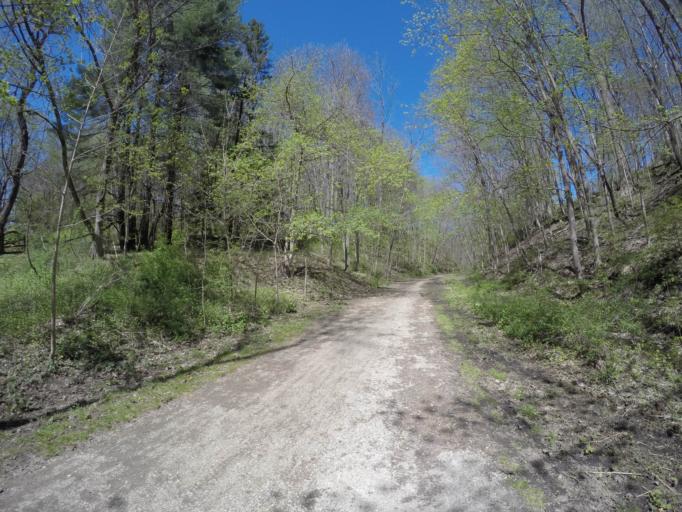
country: US
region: Maryland
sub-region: Baltimore County
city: Hunt Valley
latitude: 39.5801
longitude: -76.6151
